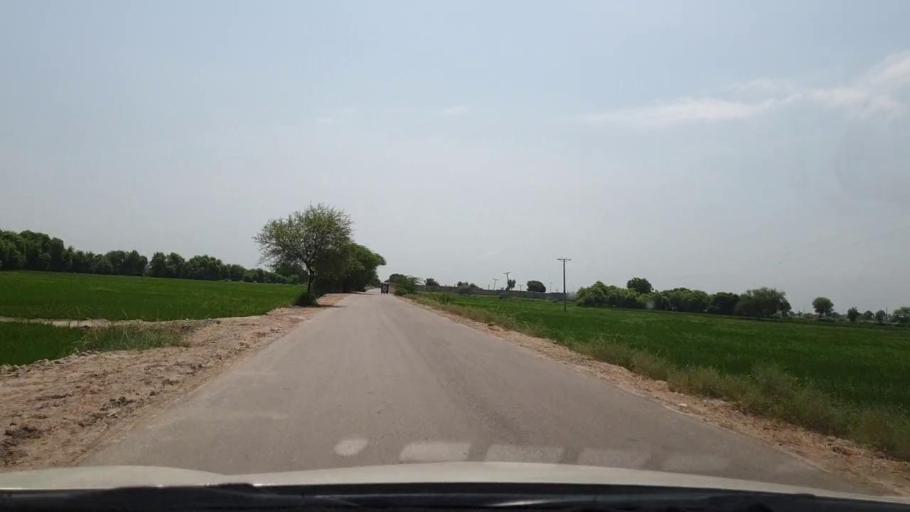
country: PK
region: Sindh
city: Ratodero
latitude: 27.8156
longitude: 68.2484
